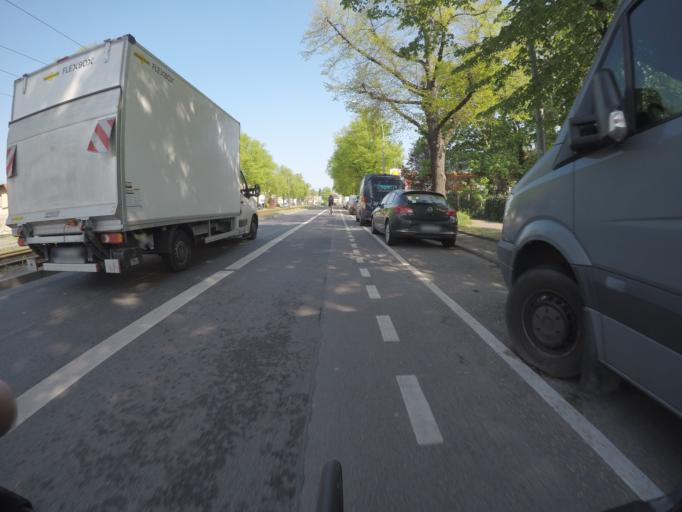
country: DE
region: Berlin
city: Buchholz
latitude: 52.6004
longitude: 13.4325
